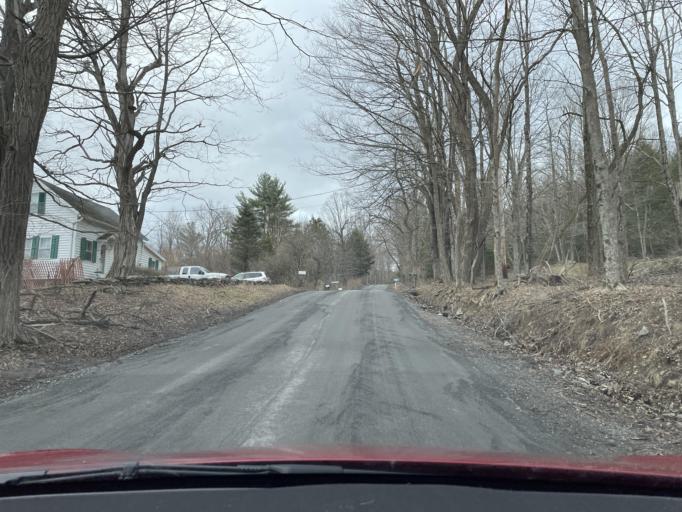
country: US
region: New York
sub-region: Ulster County
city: Woodstock
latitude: 42.0703
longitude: -74.1564
